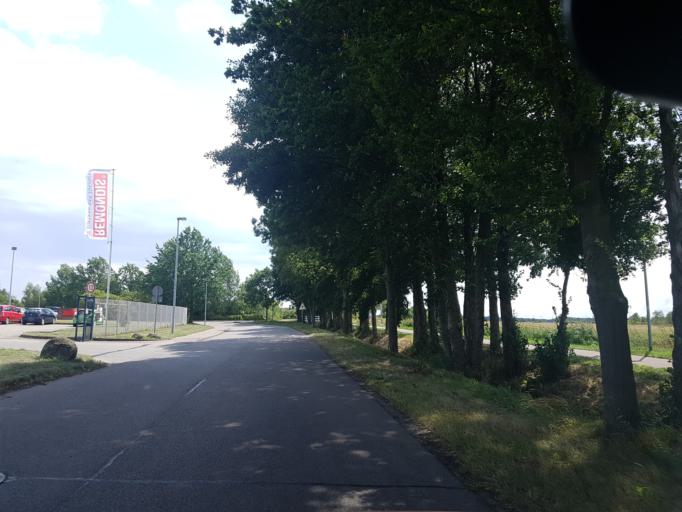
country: DE
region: Brandenburg
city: Herzberg
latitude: 51.6765
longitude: 13.2092
